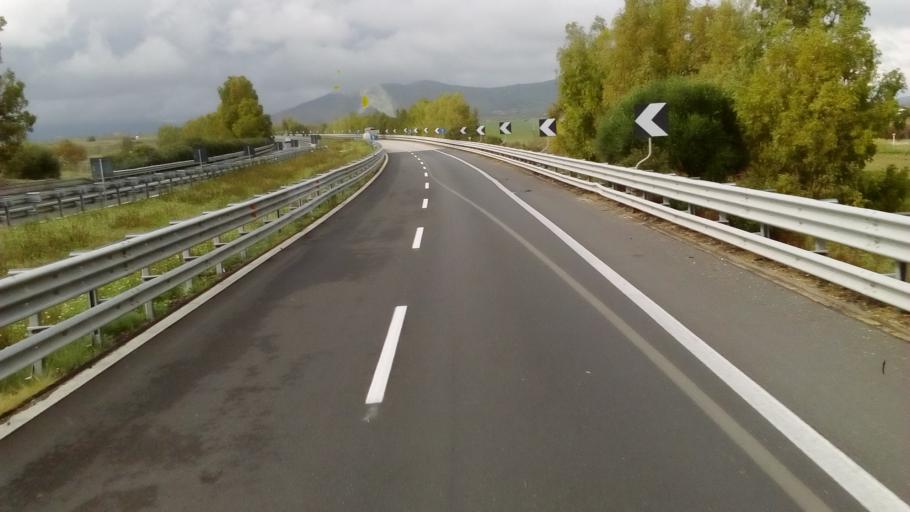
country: IT
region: Sicily
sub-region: Enna
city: Assoro
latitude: 37.5770
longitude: 14.4359
